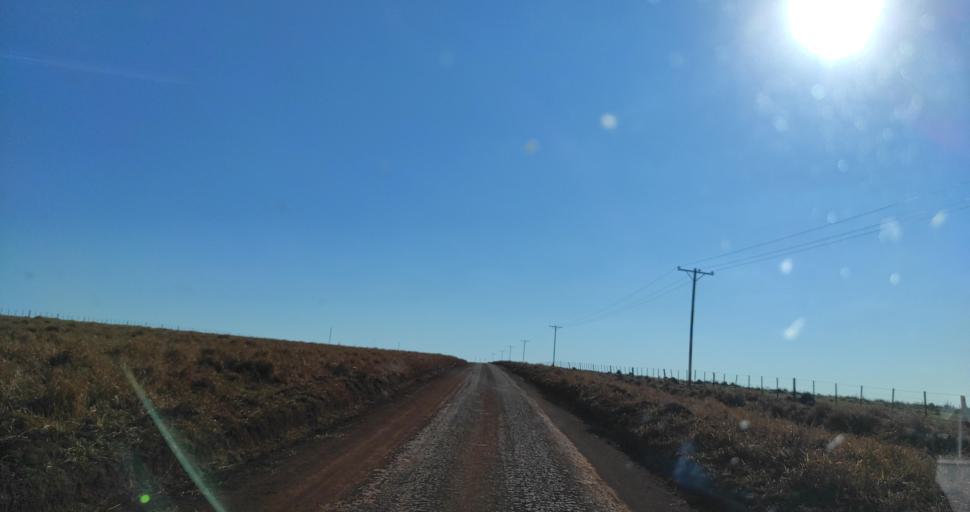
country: PY
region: Itapua
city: San Juan del Parana
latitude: -27.4363
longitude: -56.0688
